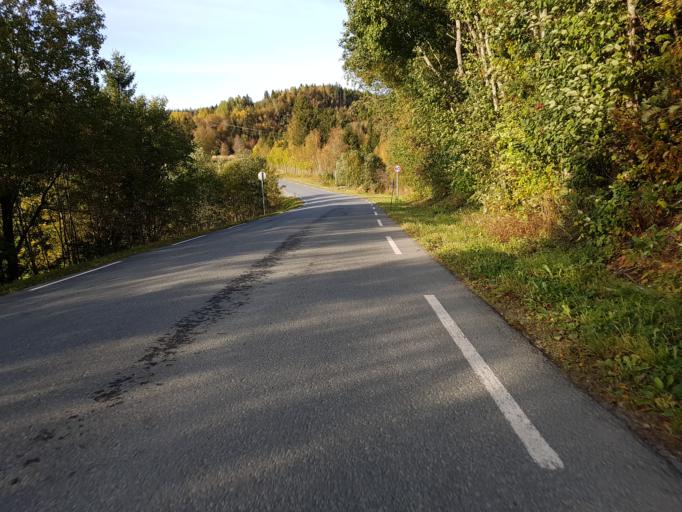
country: NO
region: Sor-Trondelag
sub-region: Klaebu
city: Klaebu
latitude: 63.3446
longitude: 10.5160
